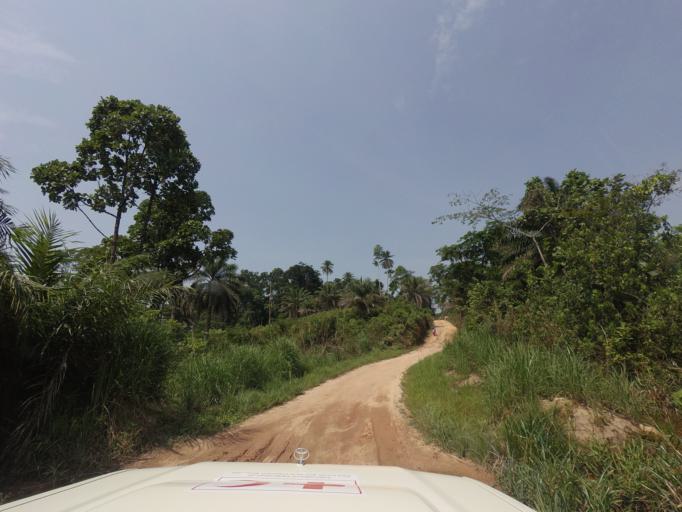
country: LR
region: Lofa
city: Voinjama
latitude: 8.5064
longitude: -9.6353
